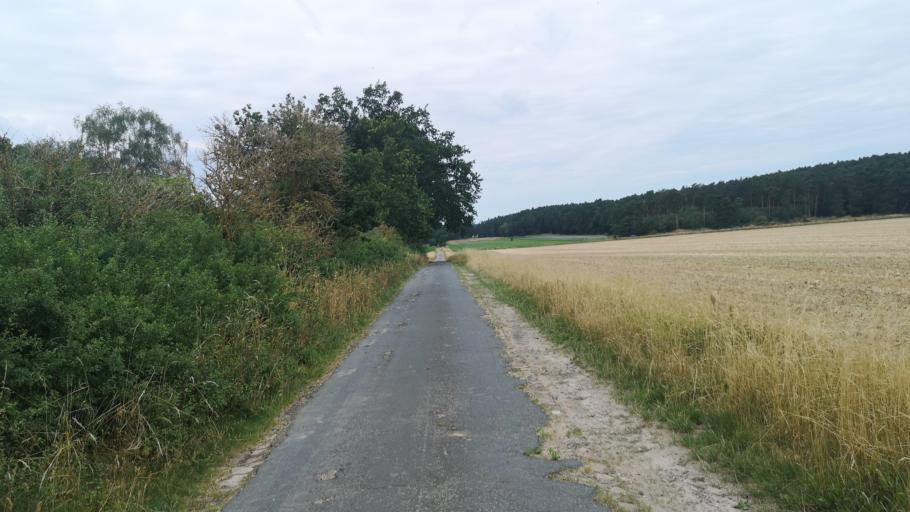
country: DE
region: Lower Saxony
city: Dahlem
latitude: 53.2155
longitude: 10.7503
